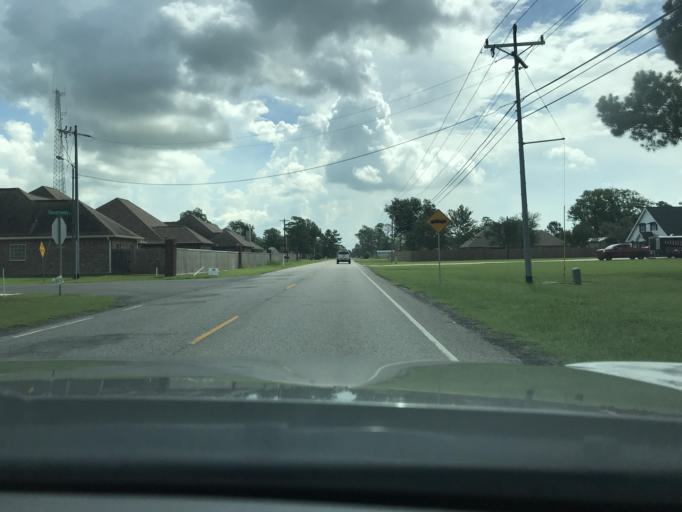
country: US
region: Louisiana
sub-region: Calcasieu Parish
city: Moss Bluff
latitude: 30.3447
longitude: -93.2267
